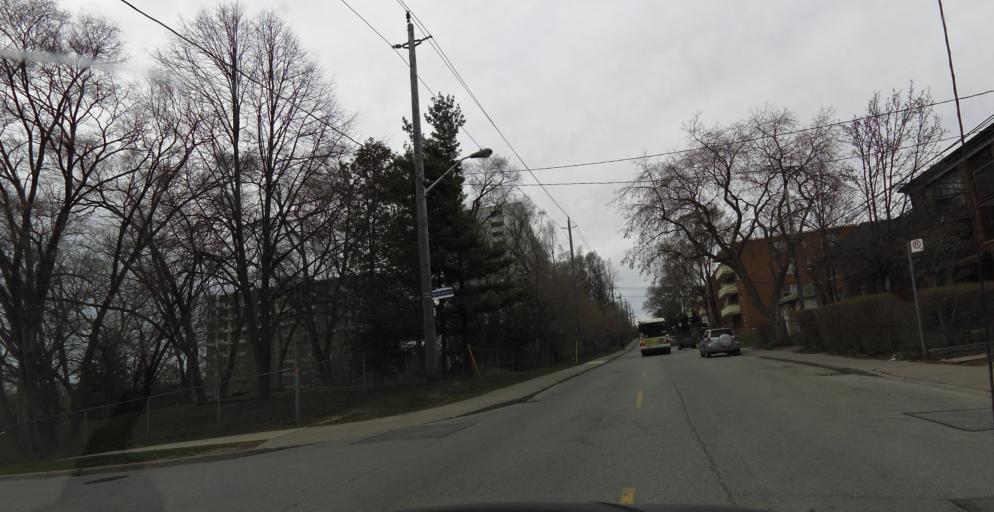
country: CA
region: Ontario
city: Toronto
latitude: 43.6382
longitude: -79.4710
